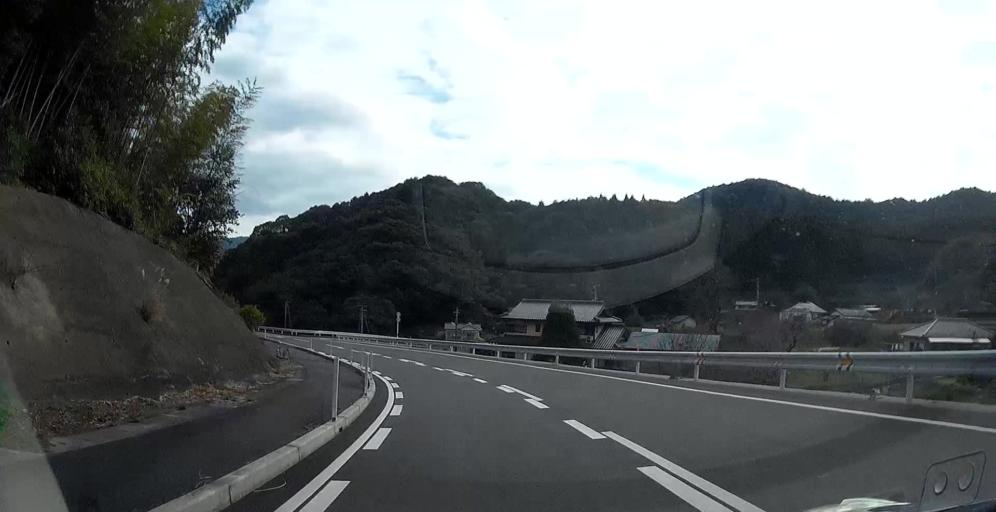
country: JP
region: Kumamoto
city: Minamata
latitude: 32.2310
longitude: 130.4269
